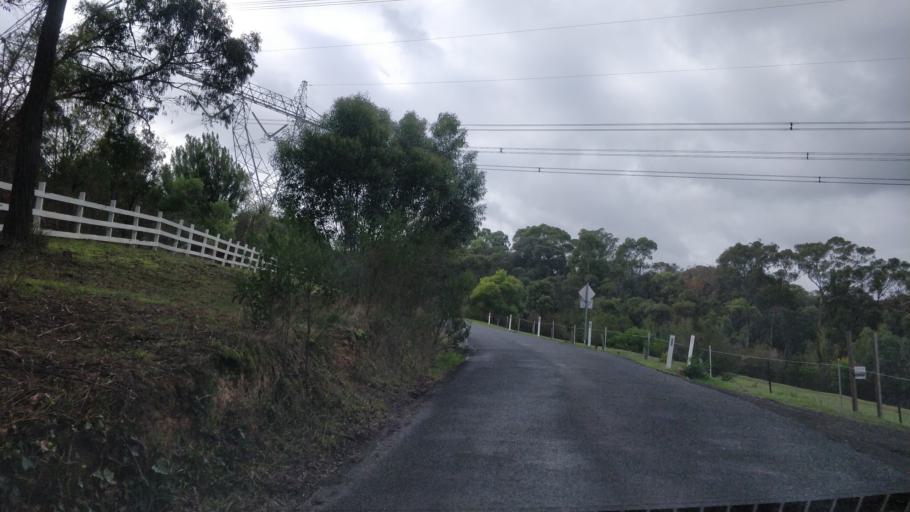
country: AU
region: Victoria
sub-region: Nillumbik
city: Research
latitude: -37.7167
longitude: 145.1706
